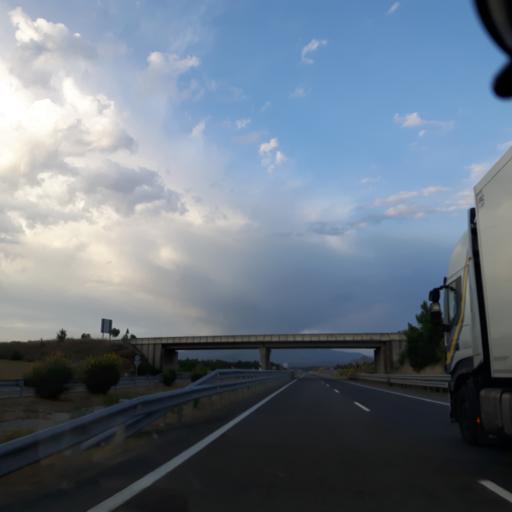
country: ES
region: Castille and Leon
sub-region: Provincia de Salamanca
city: Fuentes de Bejar
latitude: 40.5240
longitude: -5.6717
